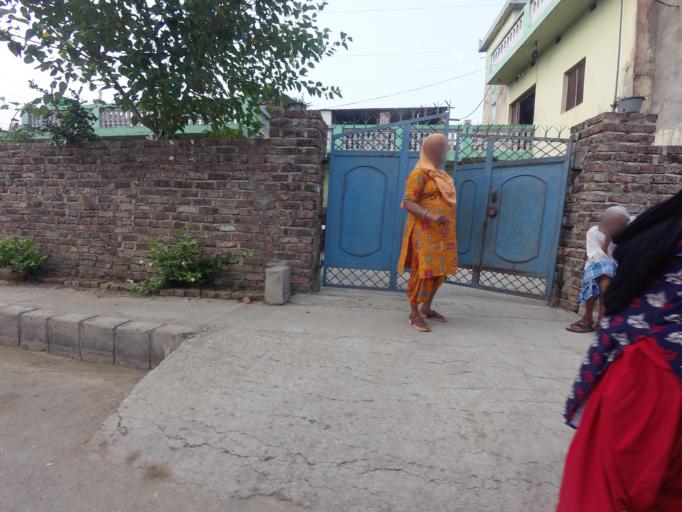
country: NP
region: Western Region
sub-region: Lumbini Zone
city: Bhairahawa
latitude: 27.4972
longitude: 83.4504
